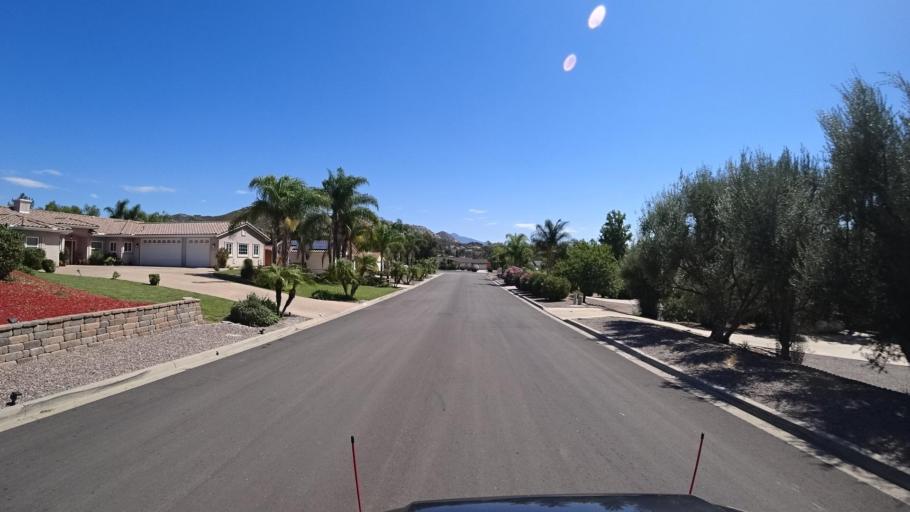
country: US
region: California
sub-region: San Diego County
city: San Diego Country Estates
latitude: 33.0201
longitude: -116.8075
